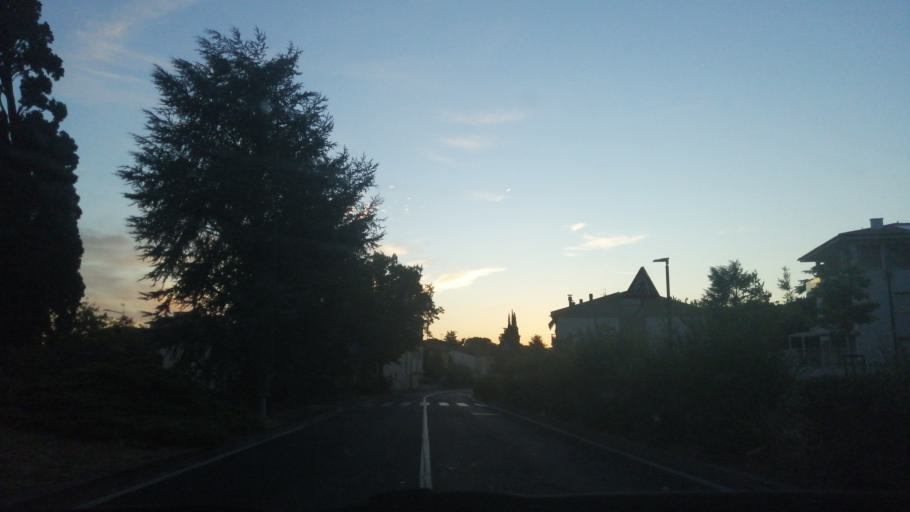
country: IT
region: Tuscany
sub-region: Province of Florence
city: Sesto Fiorentino
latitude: 43.8391
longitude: 11.2033
